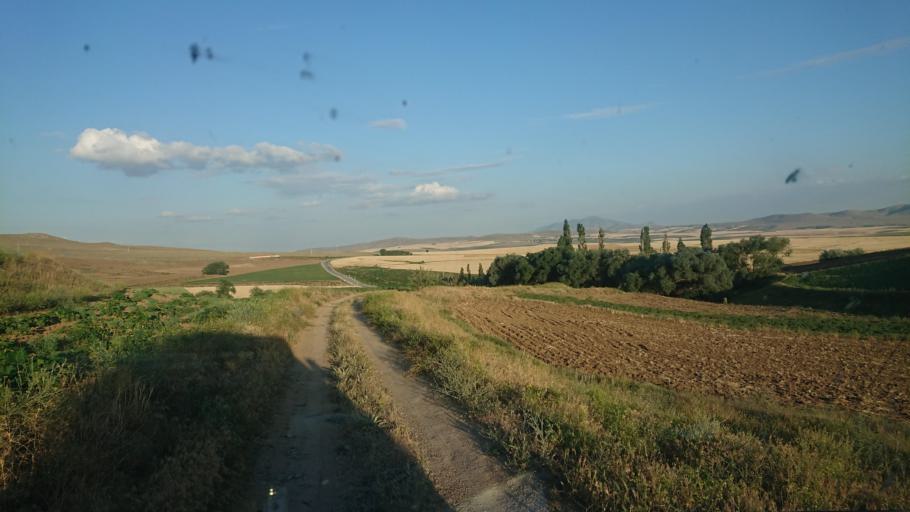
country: TR
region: Aksaray
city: Agacoren
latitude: 38.8309
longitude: 33.8862
